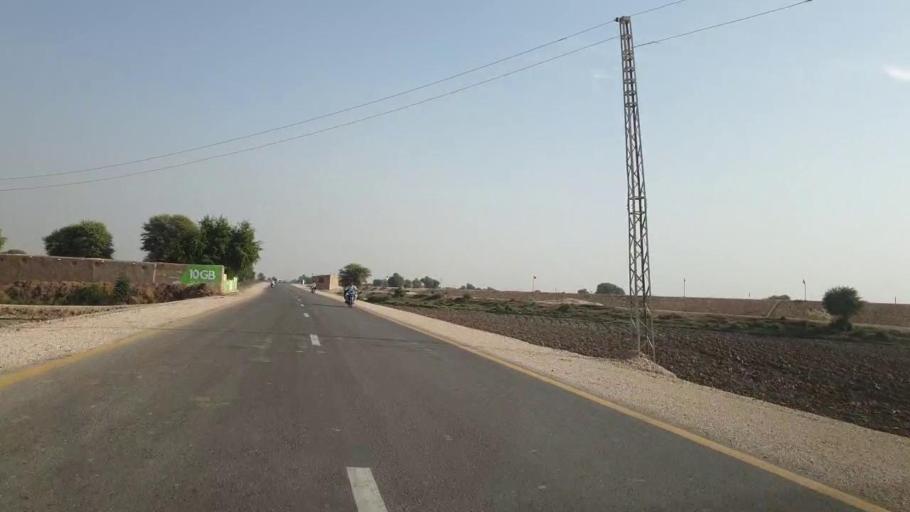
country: PK
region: Sindh
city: Sehwan
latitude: 26.4563
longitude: 67.8071
